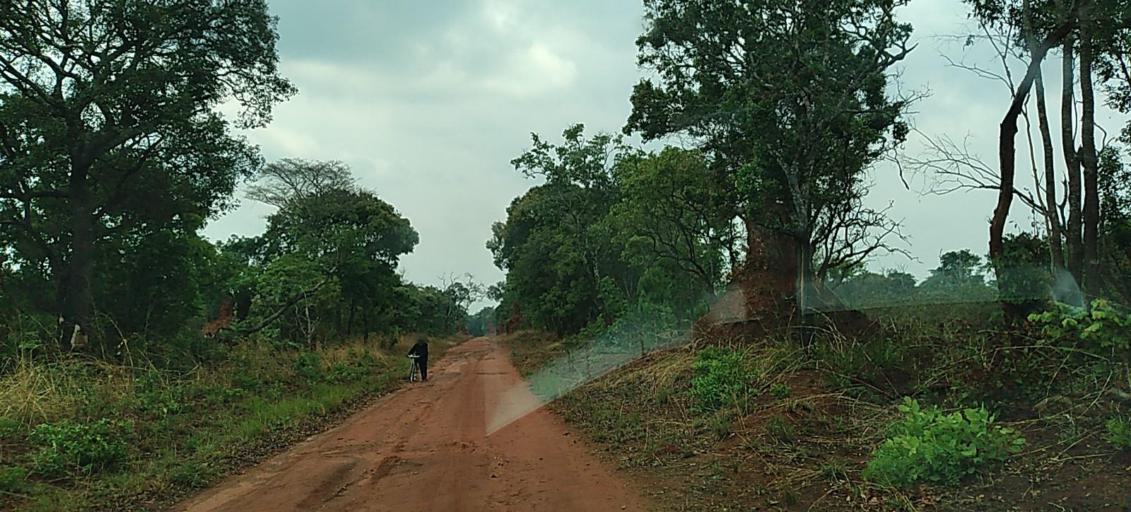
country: ZM
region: North-Western
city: Mwinilunga
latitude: -11.5456
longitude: 24.7776
